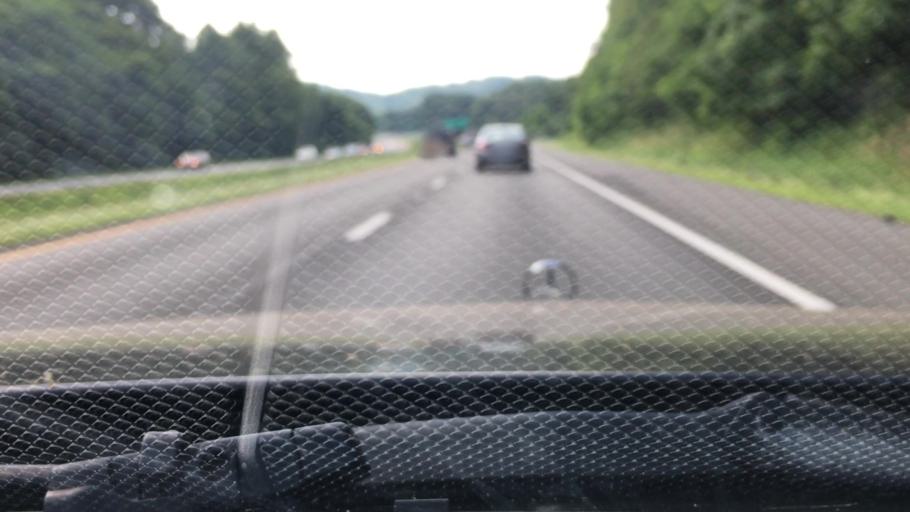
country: US
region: Virginia
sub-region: City of Charlottesville
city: Charlottesville
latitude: 38.0172
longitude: -78.5311
